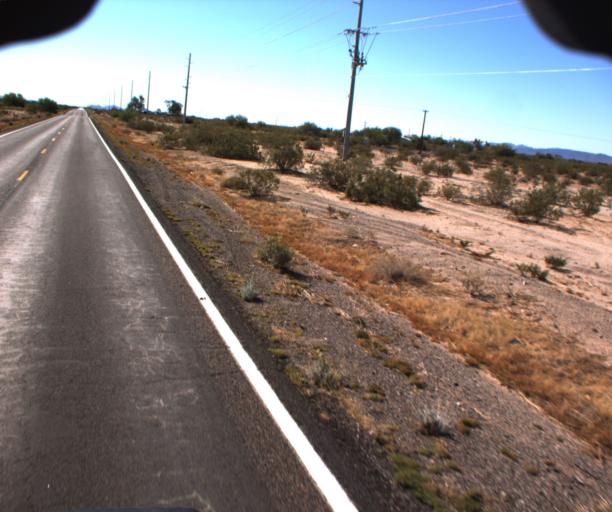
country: US
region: Arizona
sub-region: La Paz County
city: Salome
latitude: 33.8708
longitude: -113.9319
